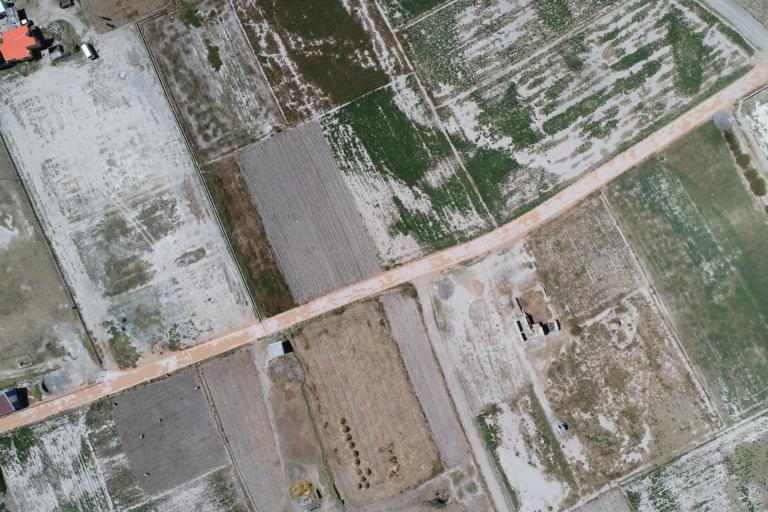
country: BO
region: La Paz
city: Achacachi
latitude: -16.0177
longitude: -68.7206
